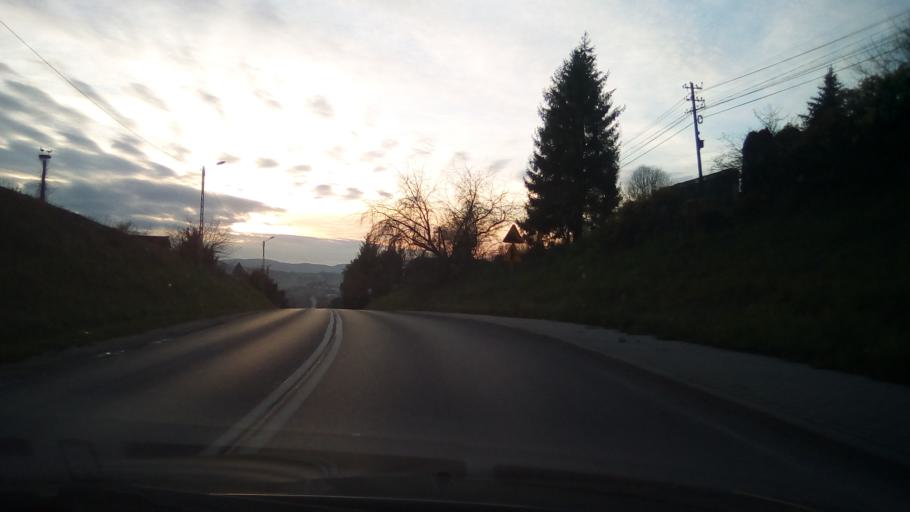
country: PL
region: Subcarpathian Voivodeship
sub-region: Powiat strzyzowski
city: Strzyzow
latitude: 49.8745
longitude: 21.8066
